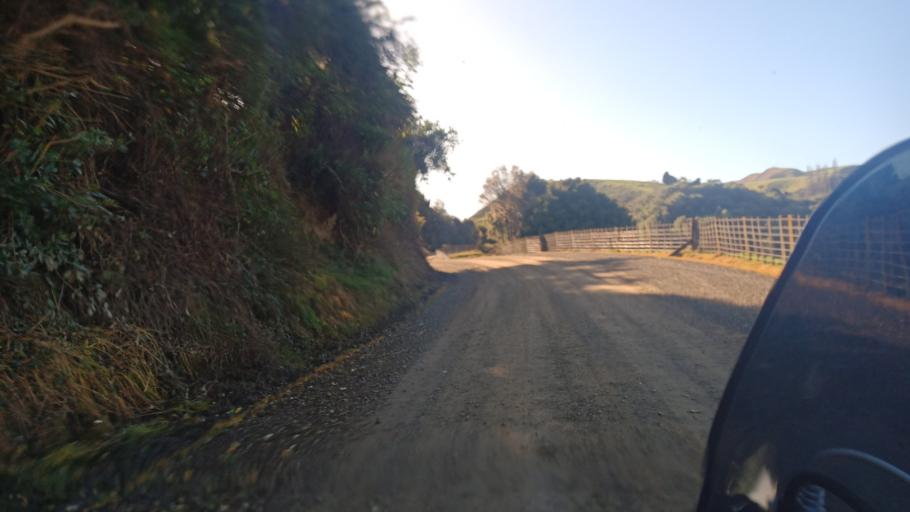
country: NZ
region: Hawke's Bay
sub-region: Wairoa District
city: Wairoa
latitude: -38.8133
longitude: 177.2897
